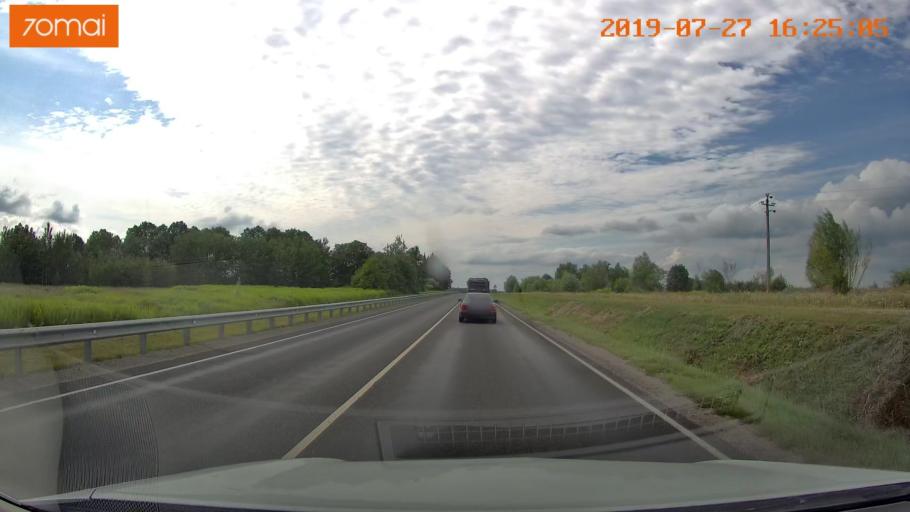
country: RU
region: Kaliningrad
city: Zheleznodorozhnyy
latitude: 54.6362
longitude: 21.4388
